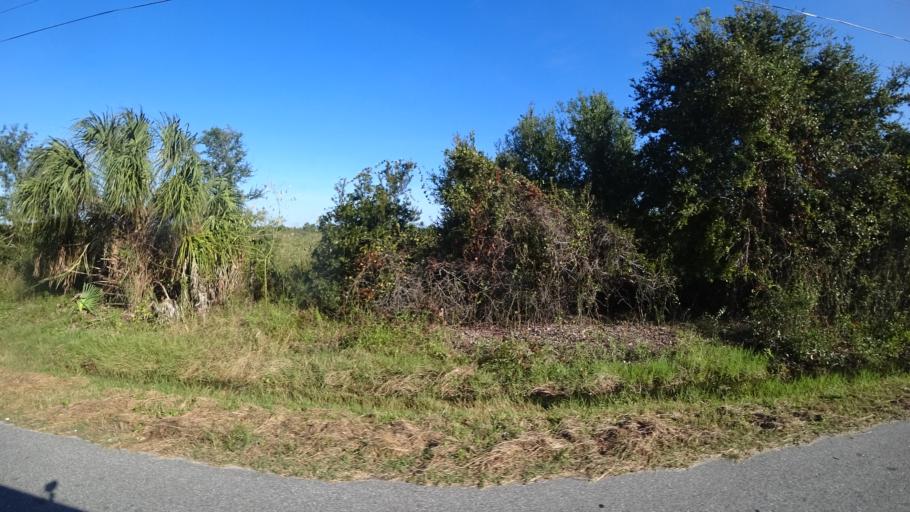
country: US
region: Florida
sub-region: Manatee County
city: Memphis
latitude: 27.6455
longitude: -82.5388
